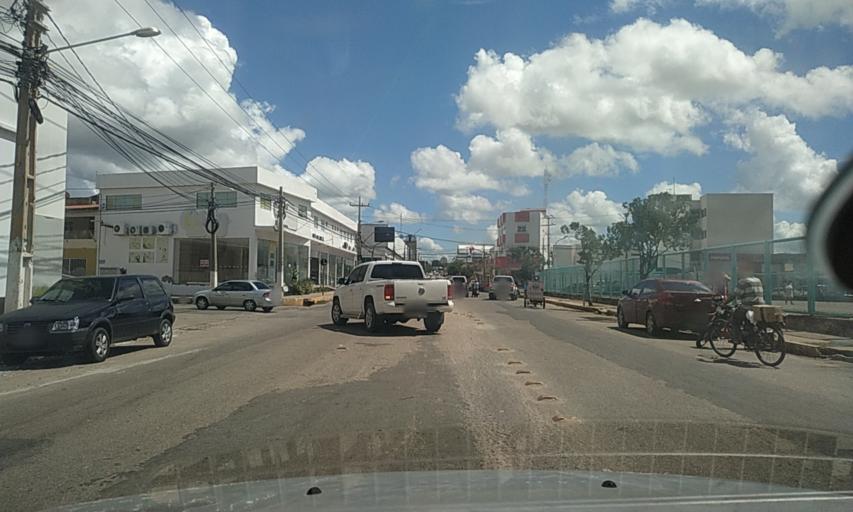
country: BR
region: Rio Grande do Norte
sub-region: Mossoro
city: Mossoro
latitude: -5.1895
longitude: -37.3377
